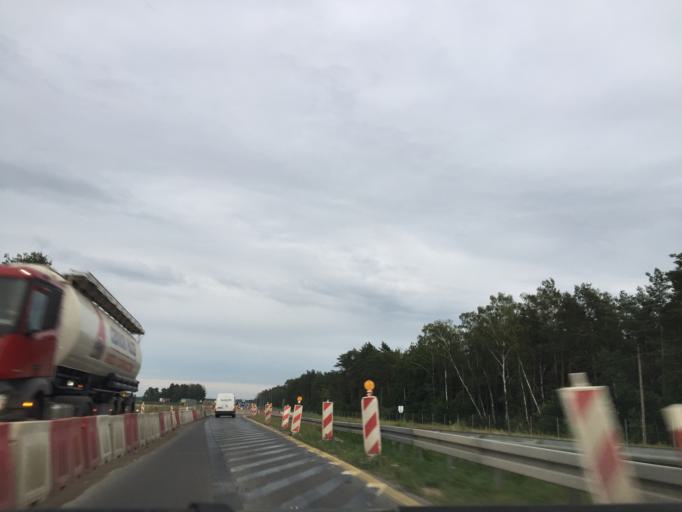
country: PL
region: Podlasie
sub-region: Powiat bialostocki
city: Tykocin
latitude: 53.1292
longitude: 22.7053
